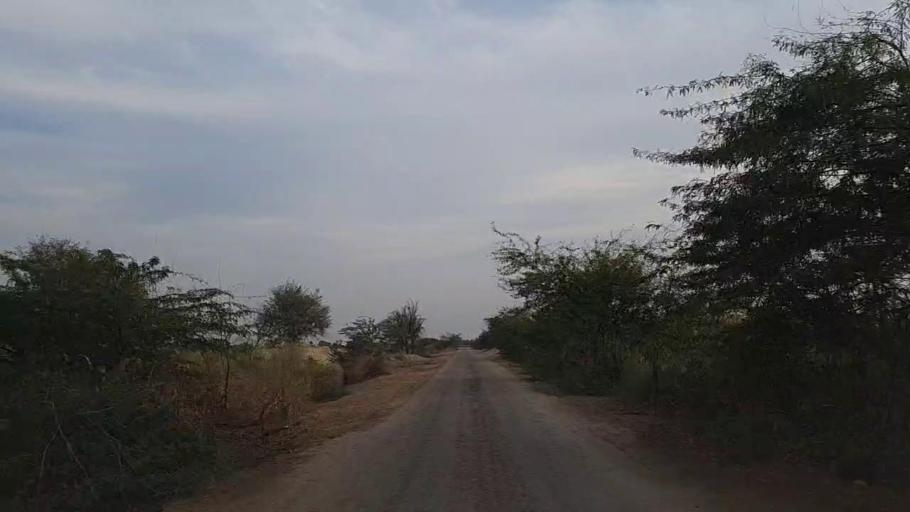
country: PK
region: Sindh
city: Jam Sahib
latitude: 26.4807
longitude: 68.5622
